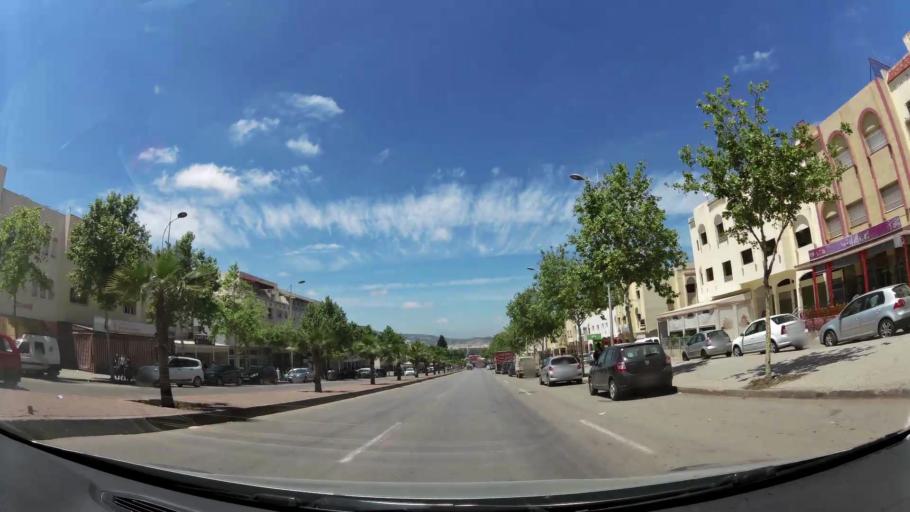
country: MA
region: Fes-Boulemane
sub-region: Fes
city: Fes
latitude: 34.0114
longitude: -4.9806
